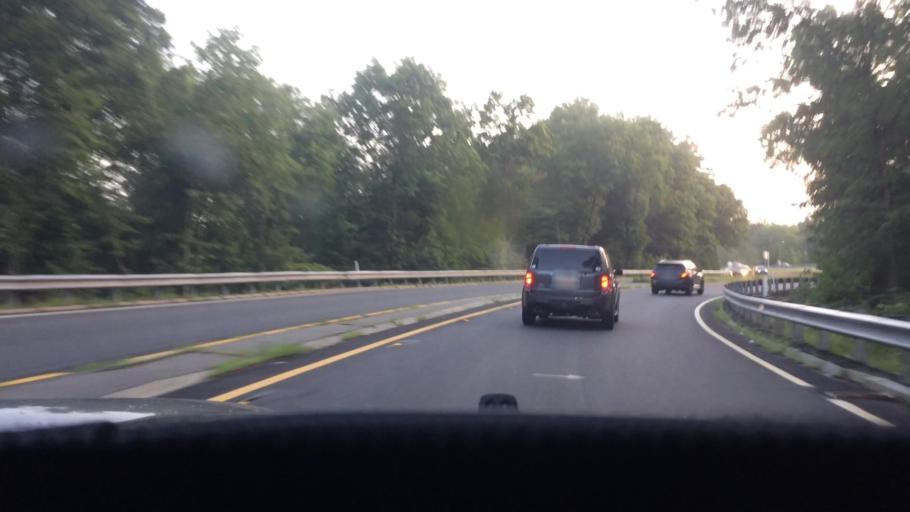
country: US
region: Massachusetts
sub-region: Middlesex County
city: Wilmington
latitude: 42.5841
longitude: -71.1606
